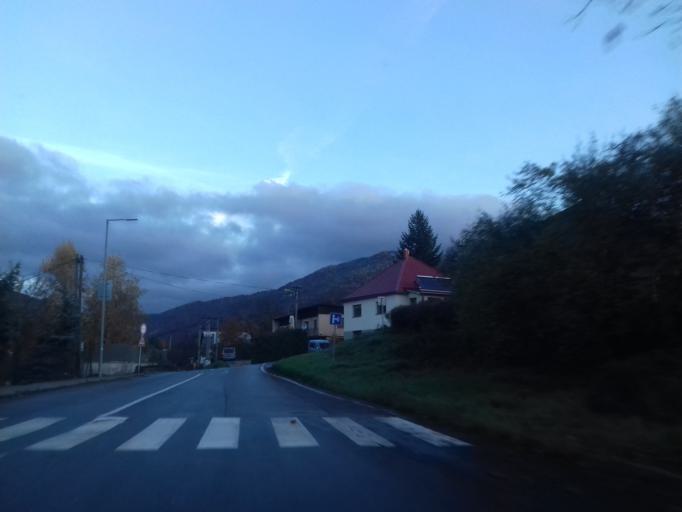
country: SK
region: Banskobystricky
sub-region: Okres Banska Bystrica
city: Banska Bystrica
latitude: 48.7563
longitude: 19.1443
